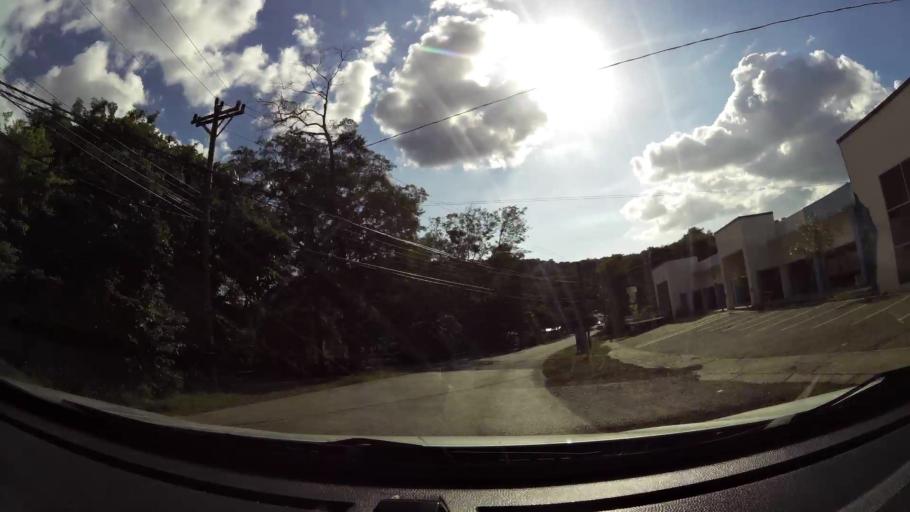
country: CR
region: Guanacaste
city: Sardinal
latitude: 10.5688
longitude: -85.6746
